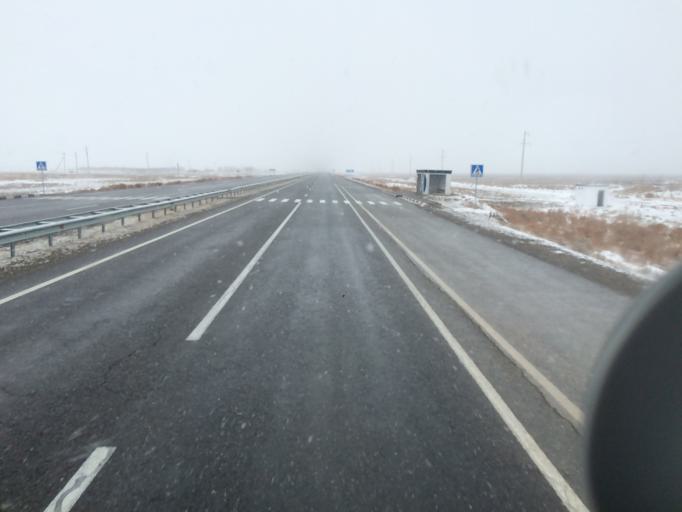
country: KZ
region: Ongtustik Qazaqstan
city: Turkestan
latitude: 43.4577
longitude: 67.9327
